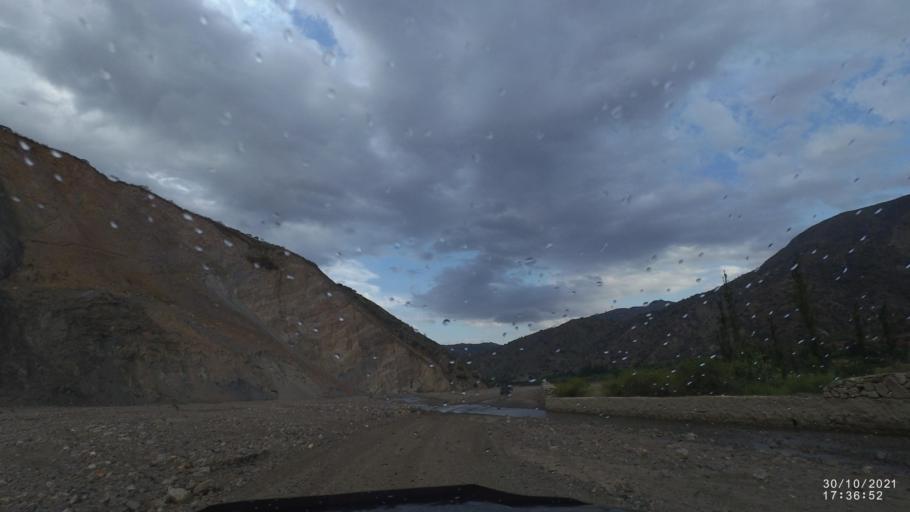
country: BO
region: Cochabamba
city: Sipe Sipe
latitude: -17.5247
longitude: -66.5633
